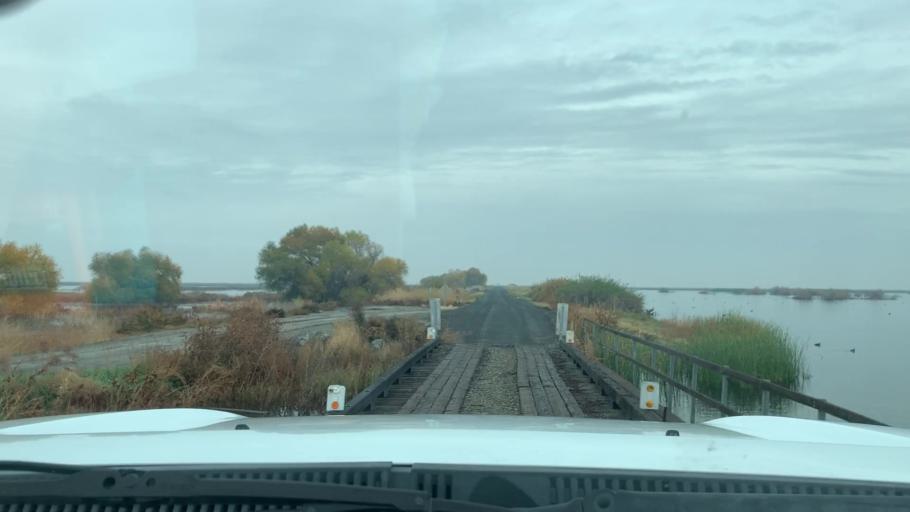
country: US
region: California
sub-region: Tulare County
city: Alpaugh
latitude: 35.7489
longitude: -119.5865
